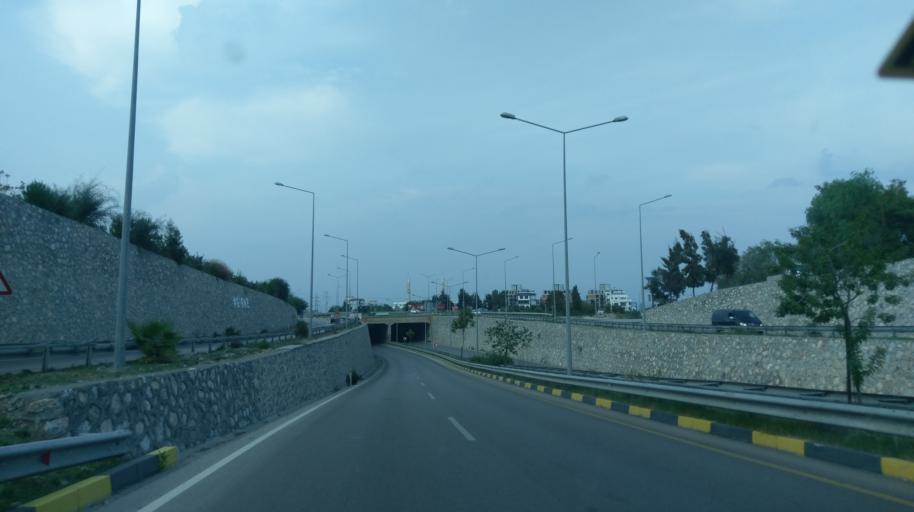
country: CY
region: Keryneia
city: Kyrenia
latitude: 35.3234
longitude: 33.3181
